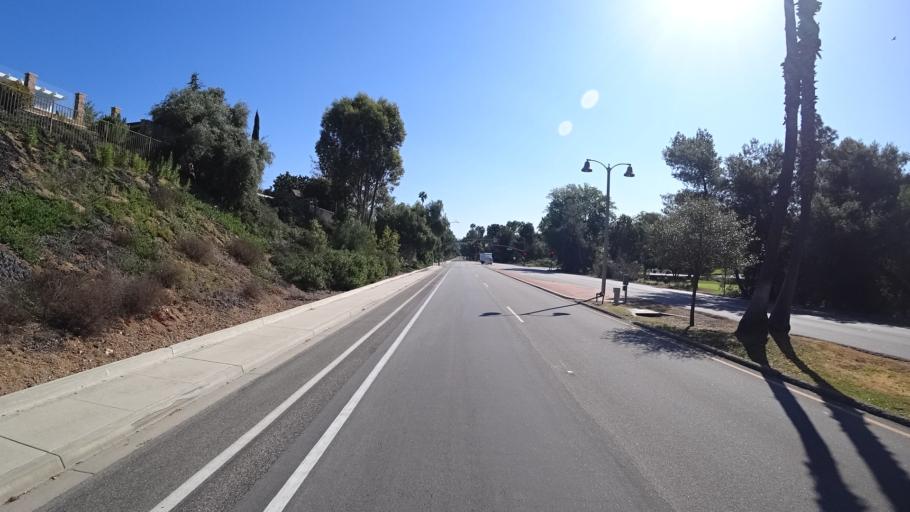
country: US
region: California
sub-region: Ventura County
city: Moorpark
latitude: 34.2383
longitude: -118.8490
